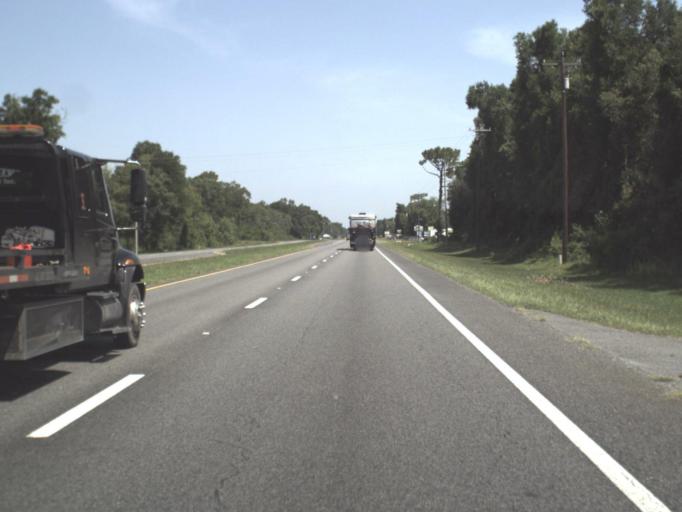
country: US
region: Florida
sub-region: Levy County
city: Manatee Road
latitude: 29.5510
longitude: -82.9003
